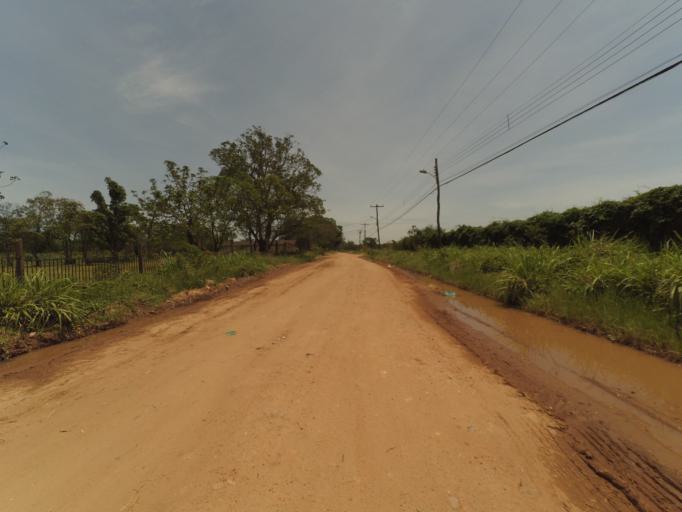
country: BO
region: Santa Cruz
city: Santa Cruz de la Sierra
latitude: -17.8343
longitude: -63.2495
